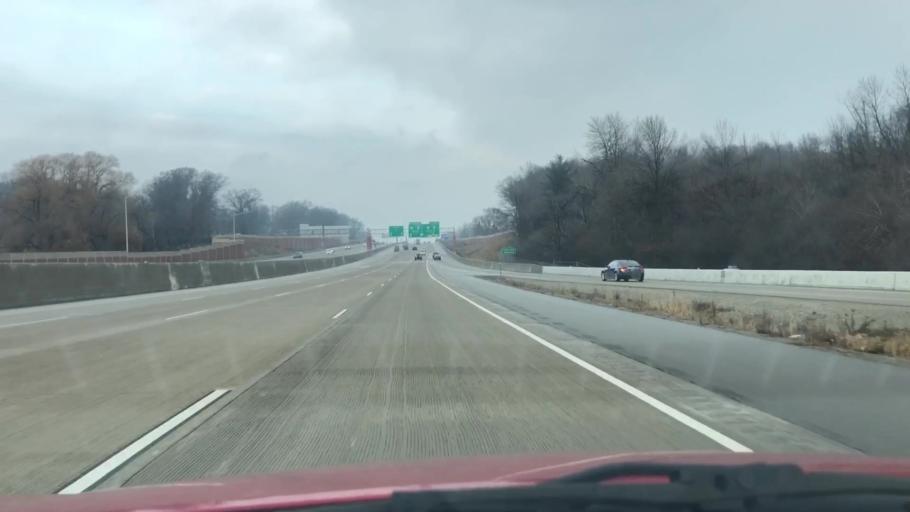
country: US
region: Wisconsin
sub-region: Brown County
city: Howard
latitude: 44.5126
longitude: -88.0824
